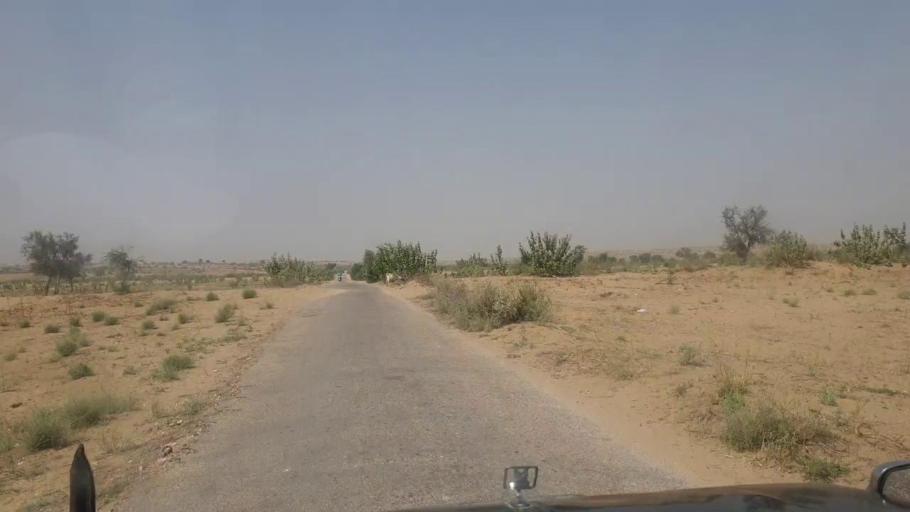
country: PK
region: Sindh
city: Islamkot
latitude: 25.1227
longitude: 70.2290
